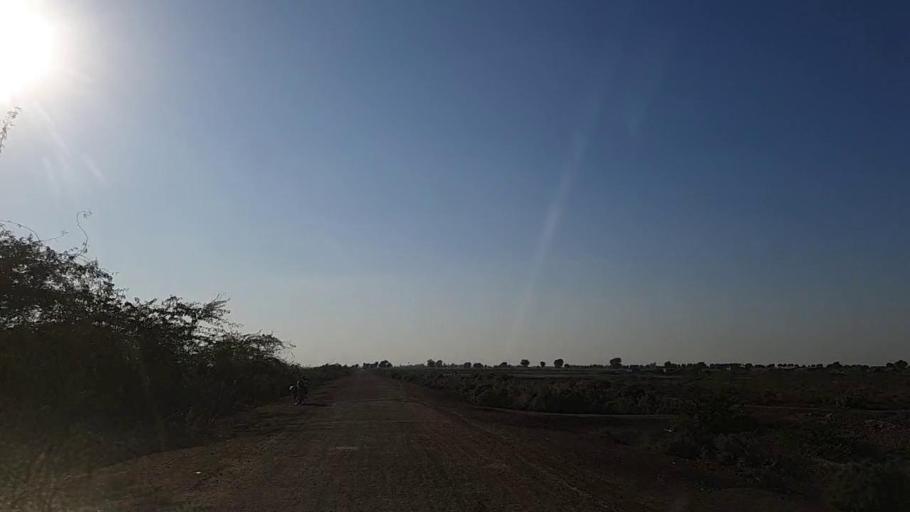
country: PK
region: Sindh
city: Samaro
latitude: 25.3441
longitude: 69.3847
